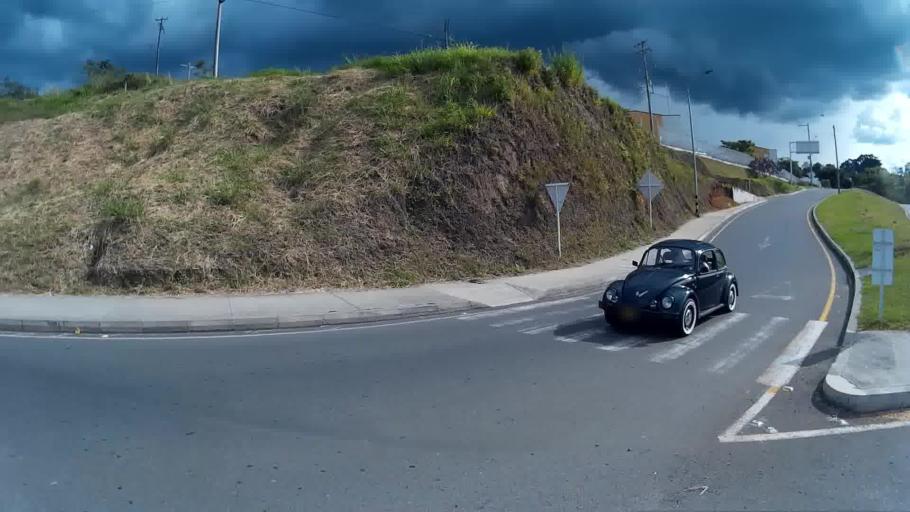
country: CO
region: Risaralda
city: Pereira
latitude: 4.8000
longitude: -75.7585
